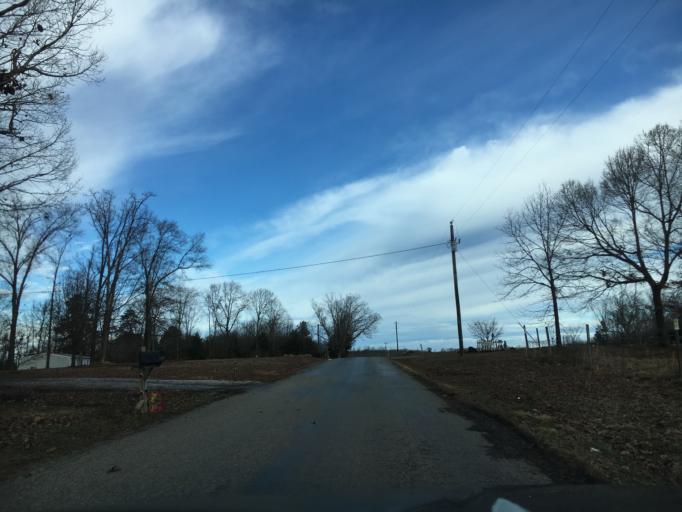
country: US
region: Virginia
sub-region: Nottoway County
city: Crewe
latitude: 37.2498
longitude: -78.2241
